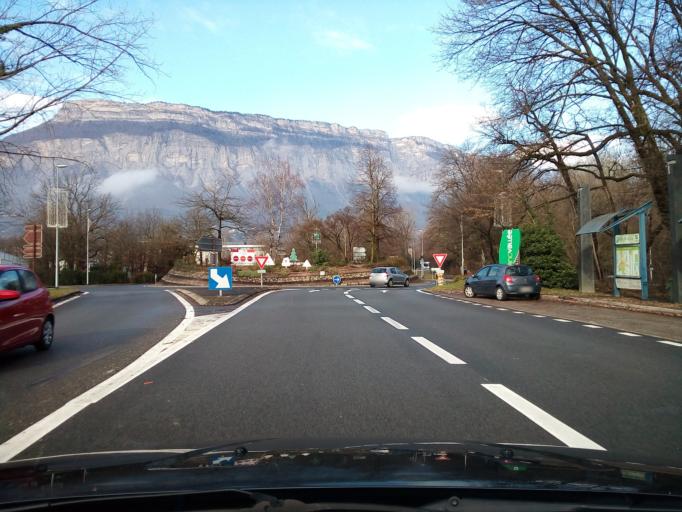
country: FR
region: Rhone-Alpes
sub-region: Departement de l'Isere
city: Meylan
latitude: 45.2084
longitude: 5.7919
